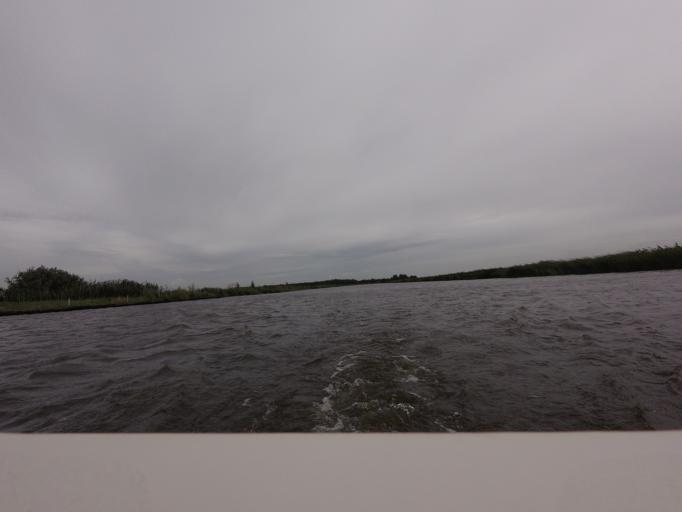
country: NL
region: Friesland
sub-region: Gemeente Boarnsterhim
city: Grou
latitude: 53.1107
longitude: 5.8699
